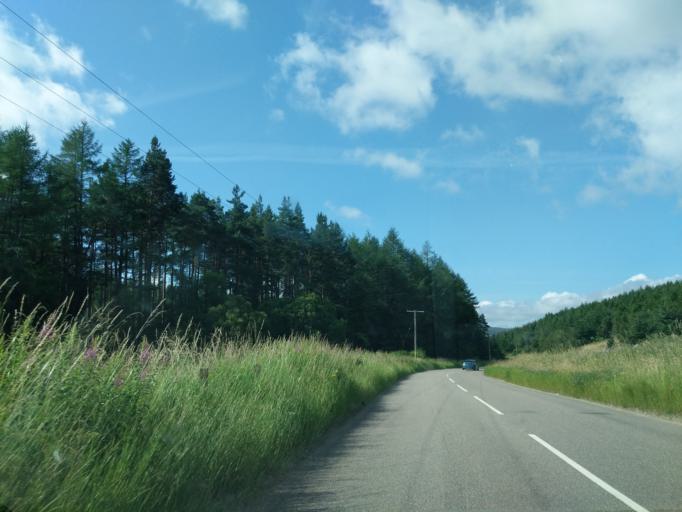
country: GB
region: Scotland
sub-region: Moray
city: Dufftown
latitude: 57.3604
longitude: -3.2829
